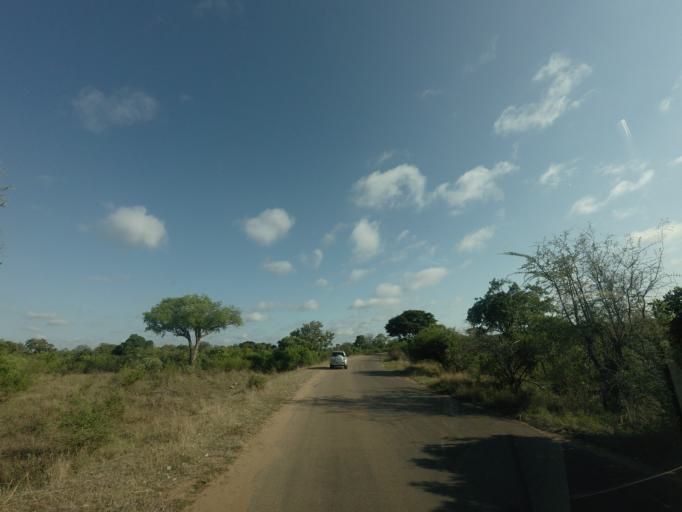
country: ZA
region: Mpumalanga
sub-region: Ehlanzeni District
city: Komatipoort
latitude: -25.2625
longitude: 31.8459
